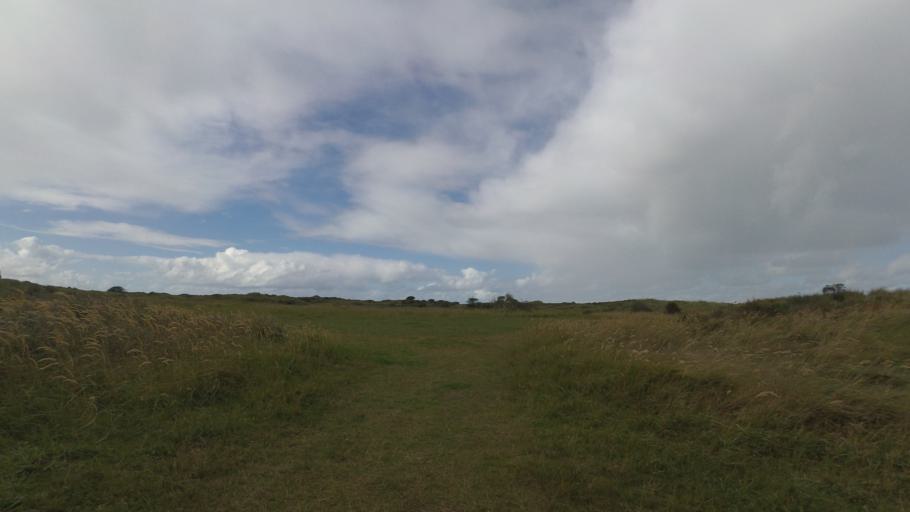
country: NL
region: Friesland
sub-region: Gemeente Ameland
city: Nes
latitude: 53.4537
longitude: 5.8384
